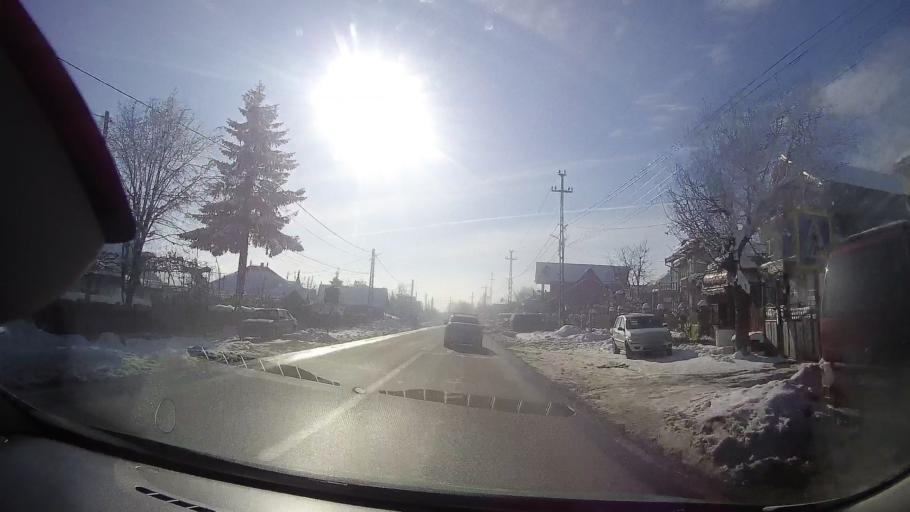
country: RO
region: Iasi
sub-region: Comuna Motca
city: Motca
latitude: 47.2492
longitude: 26.6086
